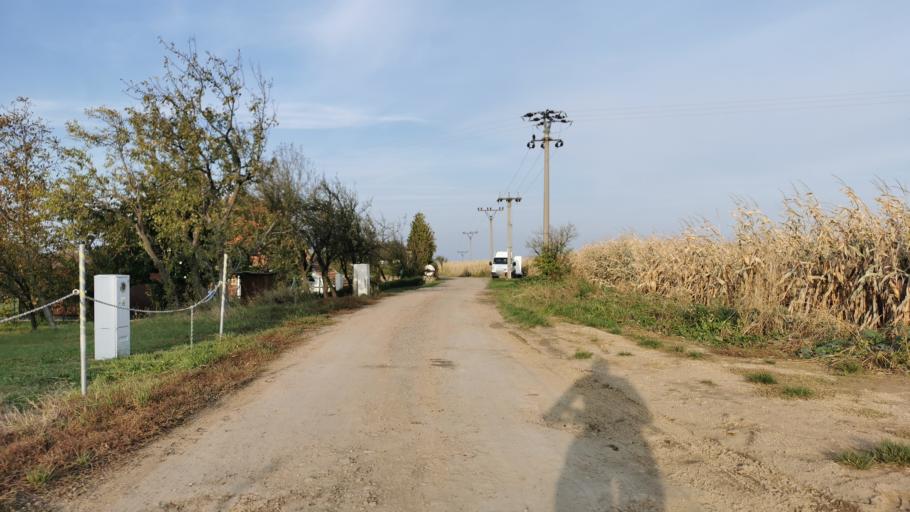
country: SK
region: Trnavsky
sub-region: Okres Skalica
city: Skalica
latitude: 48.8254
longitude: 17.2418
